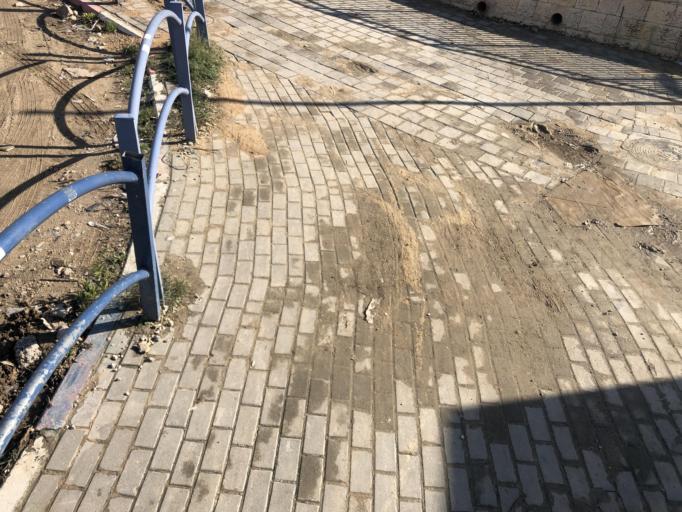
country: IL
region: Jerusalem
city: Modiin Ilit
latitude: 31.9244
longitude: 35.0459
